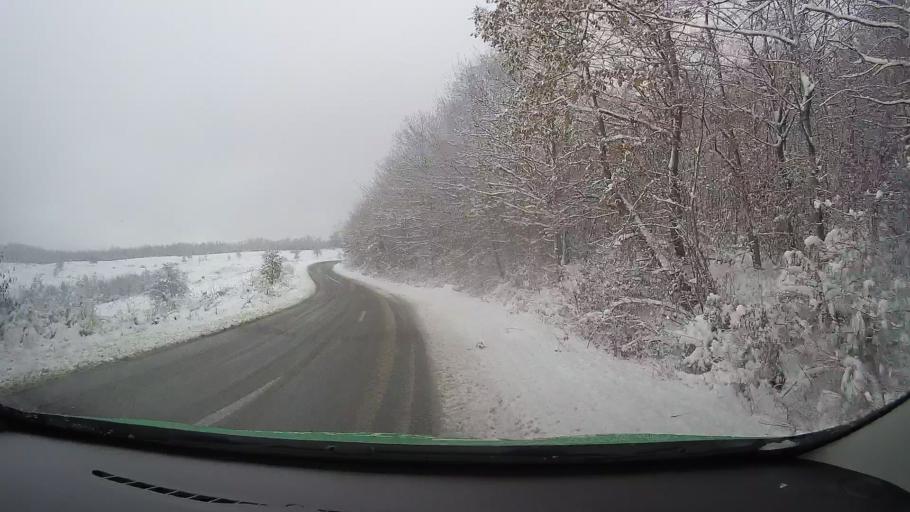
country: RO
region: Hunedoara
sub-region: Comuna Teliucu Inferior
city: Teliucu Inferior
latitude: 45.6839
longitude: 22.9101
